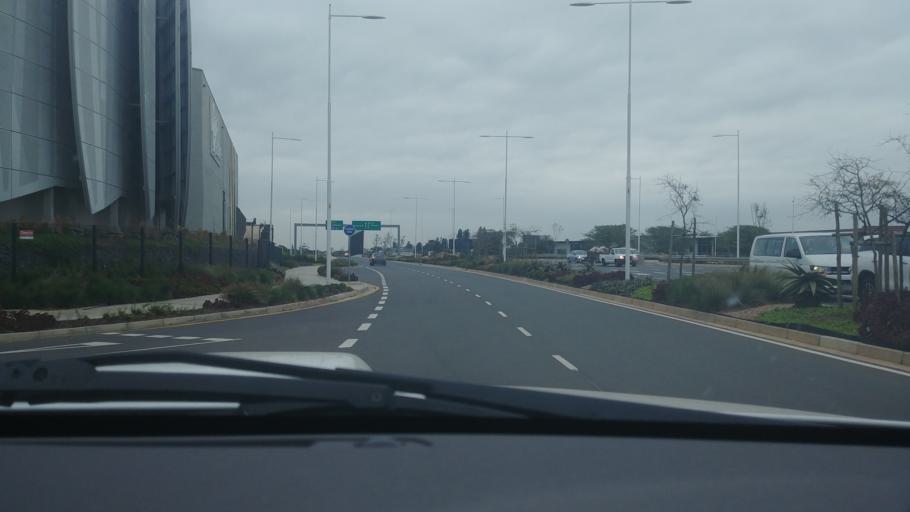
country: ZA
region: KwaZulu-Natal
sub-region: eThekwini Metropolitan Municipality
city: Durban
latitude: -29.7098
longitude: 31.0536
